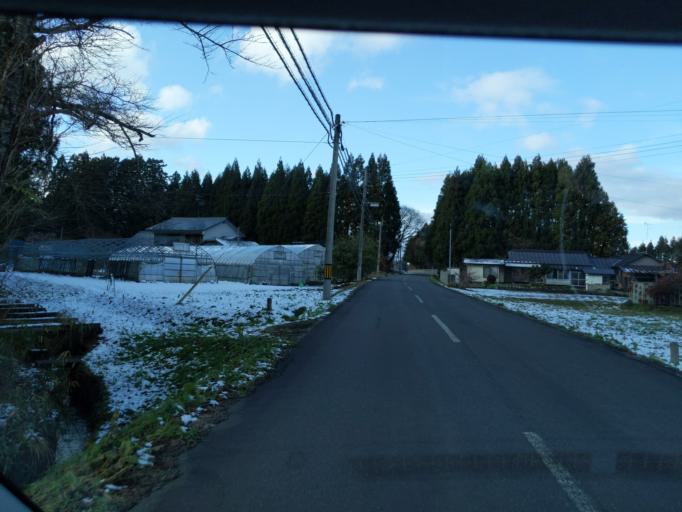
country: JP
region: Iwate
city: Kitakami
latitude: 39.2202
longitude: 141.0453
